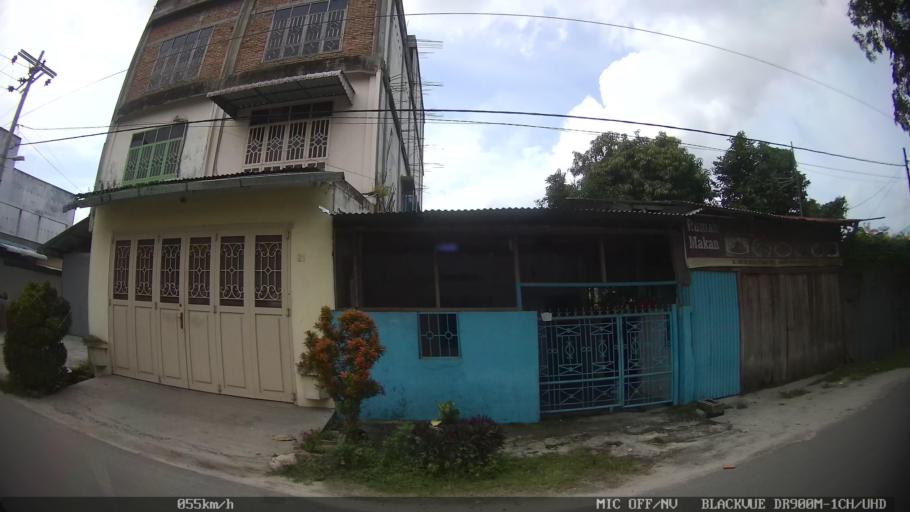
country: ID
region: North Sumatra
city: Percut
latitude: 3.5618
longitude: 98.8686
